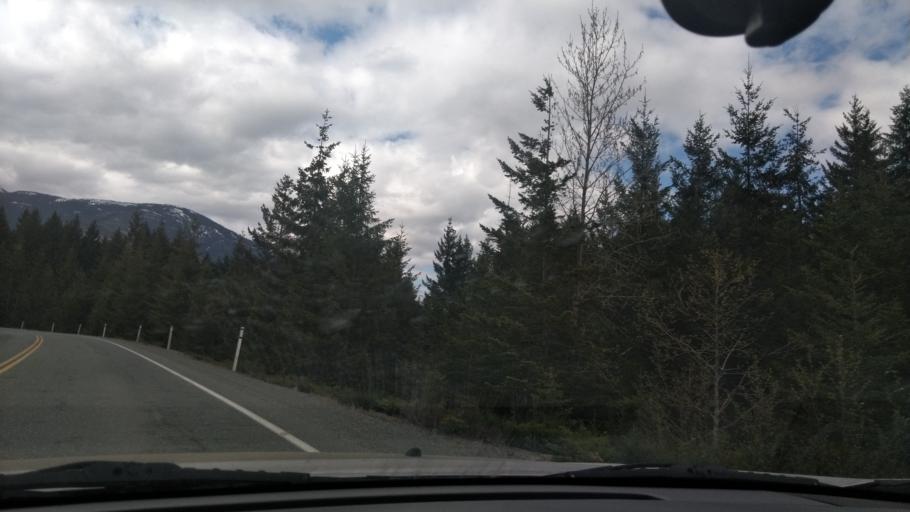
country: CA
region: British Columbia
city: Campbell River
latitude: 49.8684
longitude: -125.6478
